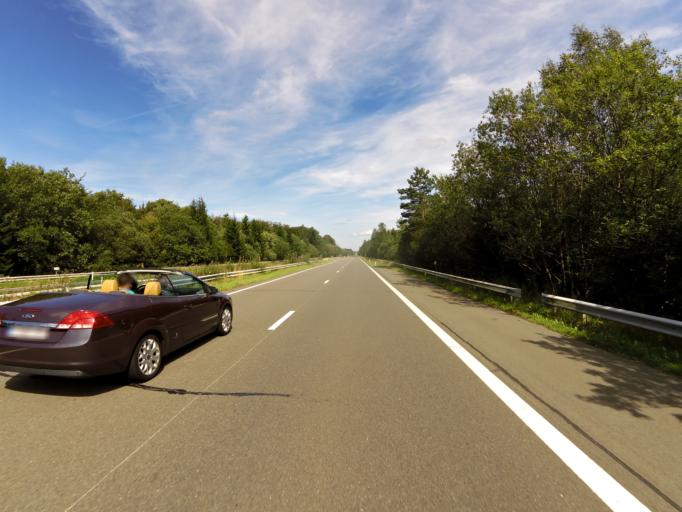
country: BE
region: Wallonia
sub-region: Province du Luxembourg
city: Saint-Hubert
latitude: 50.0630
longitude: 5.4147
